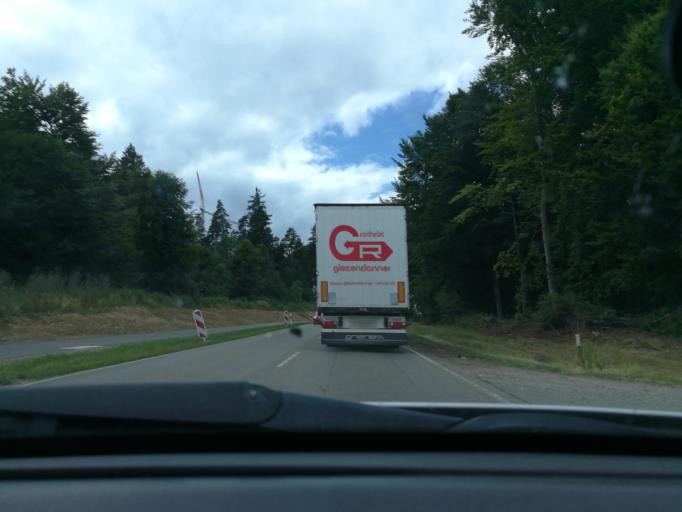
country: DE
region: Baden-Wuerttemberg
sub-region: Freiburg Region
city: Villingendorf
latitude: 48.1800
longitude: 8.5616
